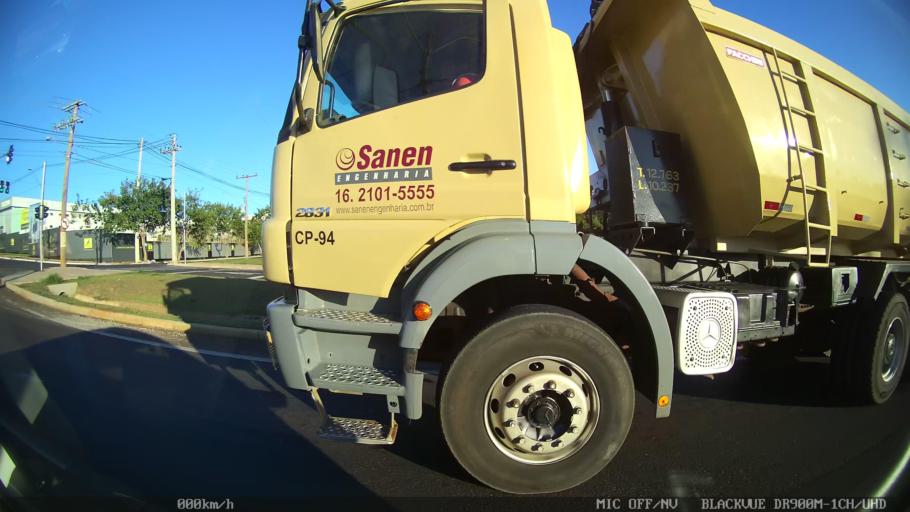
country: BR
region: Sao Paulo
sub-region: Araraquara
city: Araraquara
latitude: -21.7873
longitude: -48.2103
